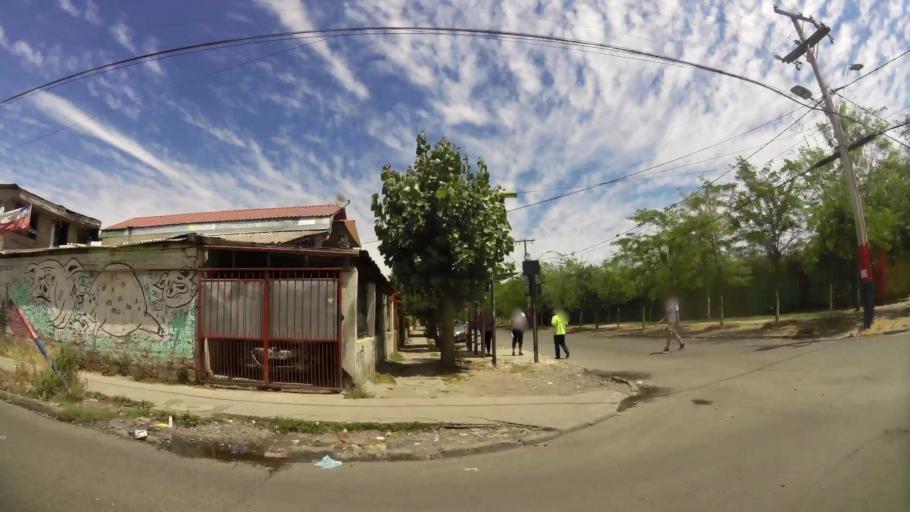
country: CL
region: Santiago Metropolitan
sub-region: Provincia de Santiago
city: La Pintana
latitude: -33.5525
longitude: -70.6445
